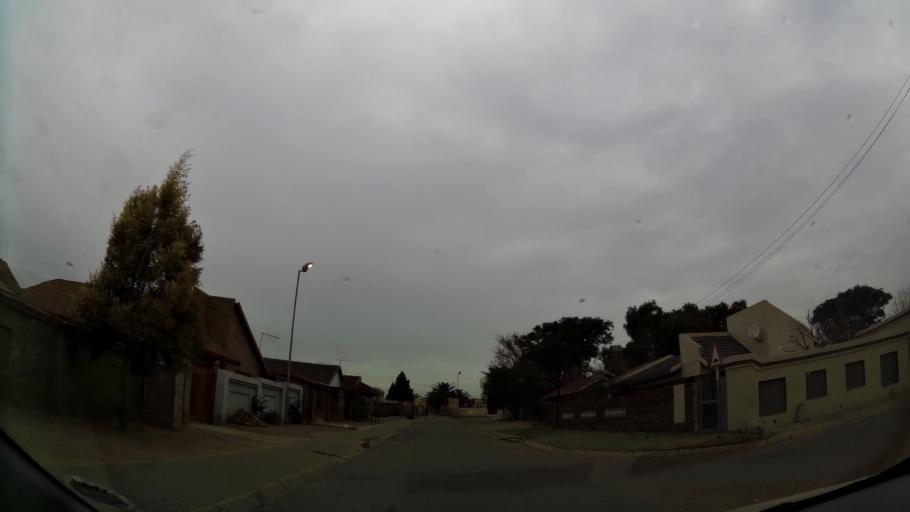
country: ZA
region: Gauteng
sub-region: City of Tshwane Metropolitan Municipality
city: Pretoria
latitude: -25.7118
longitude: 28.3415
